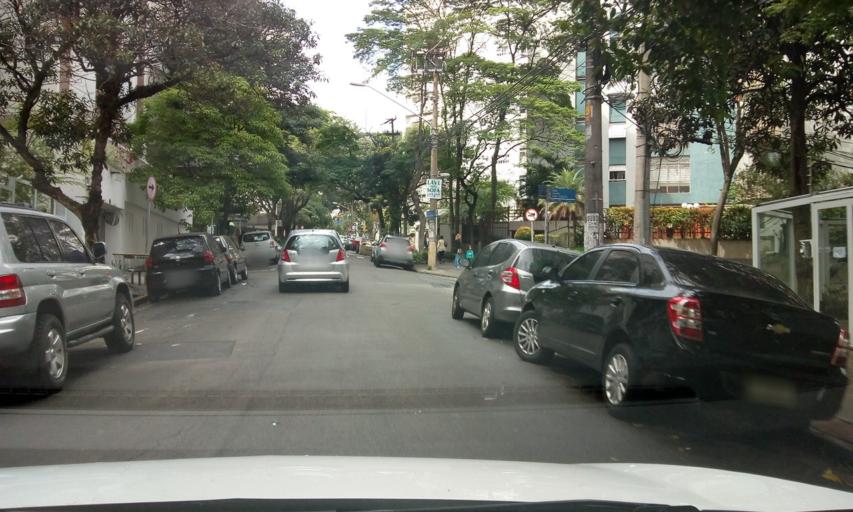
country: BR
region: Sao Paulo
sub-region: Sao Paulo
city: Sao Paulo
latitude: -23.5373
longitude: -46.6612
